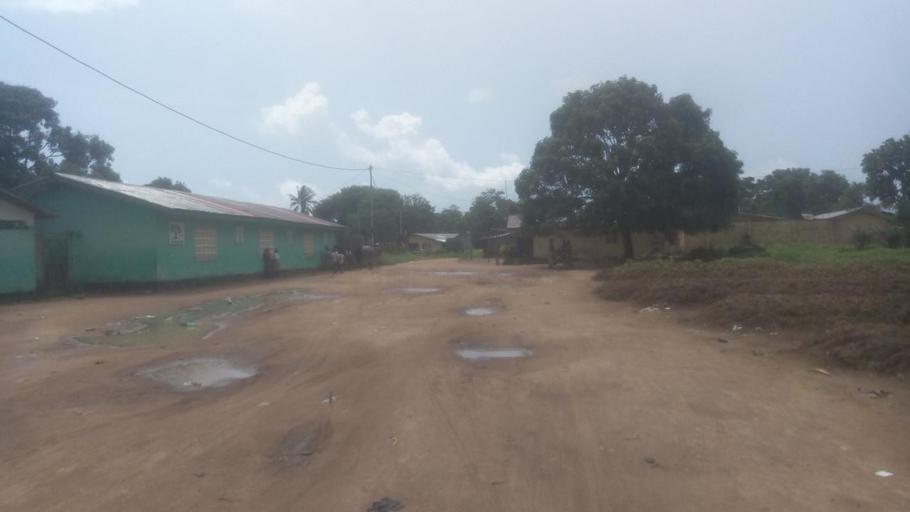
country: SL
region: Northern Province
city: Tintafor
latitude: 8.6324
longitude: -13.2172
